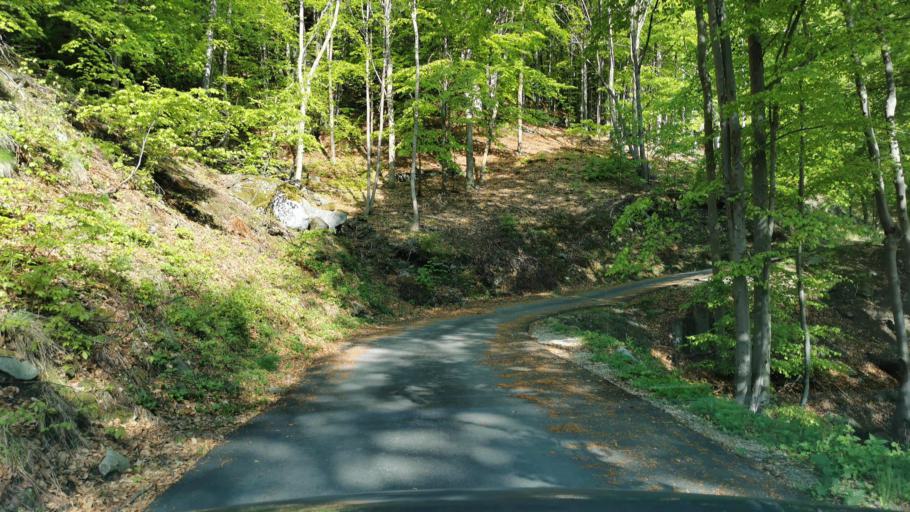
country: IT
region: Piedmont
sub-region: Provincia di Torino
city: Lemie
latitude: 45.2404
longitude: 7.2806
